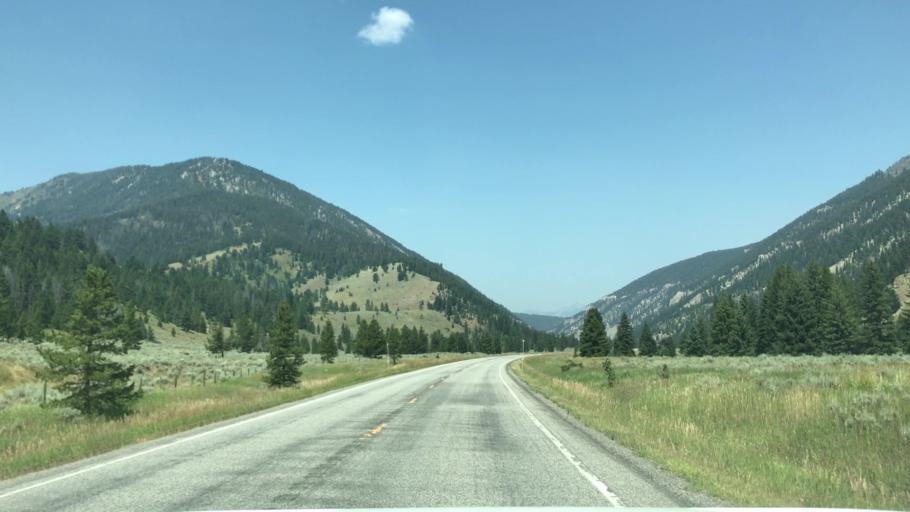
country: US
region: Montana
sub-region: Gallatin County
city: Big Sky
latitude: 45.1042
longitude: -111.2211
